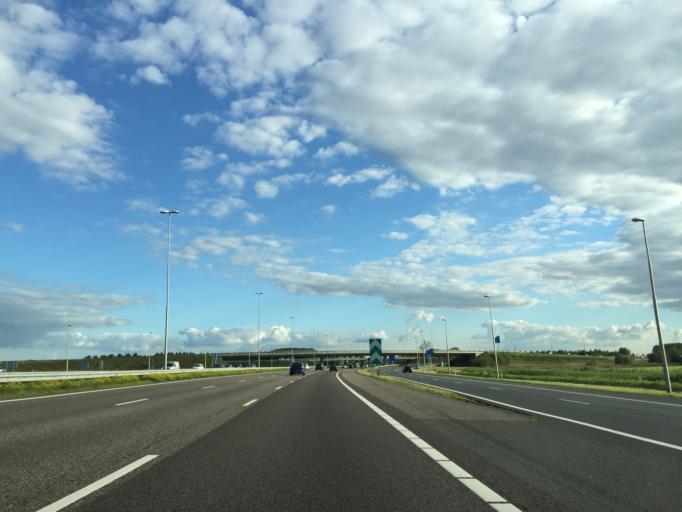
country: NL
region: South Holland
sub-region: Gemeente Strijen
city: Strijen
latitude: 51.7033
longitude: 4.6470
